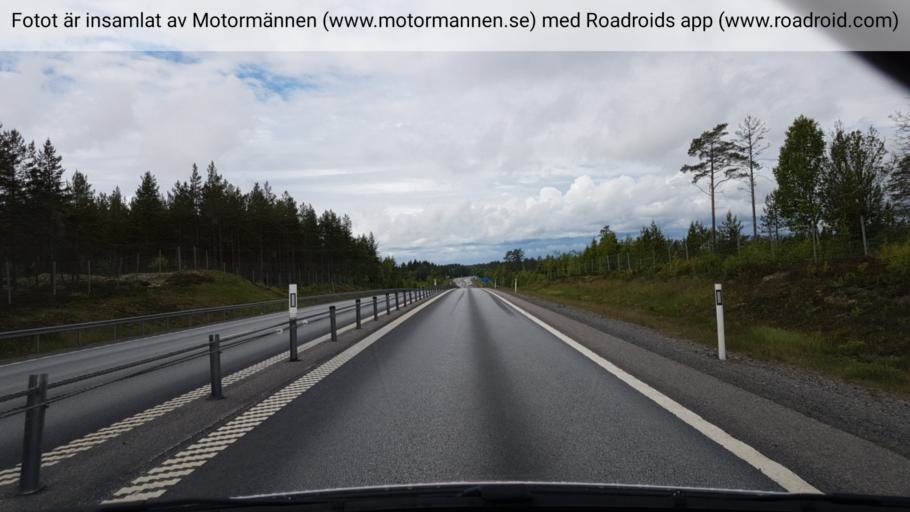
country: SE
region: Vaesterbotten
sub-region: Umea Kommun
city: Hoernefors
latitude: 63.6468
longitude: 19.9377
